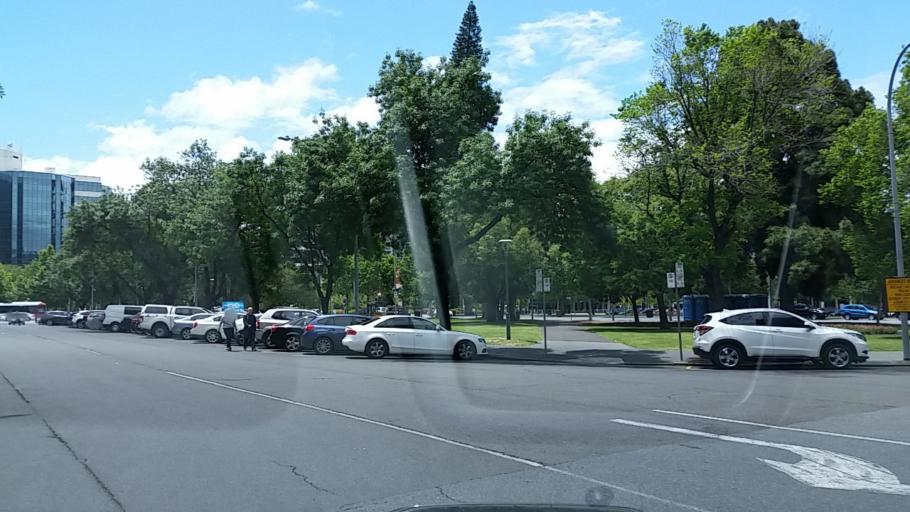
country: AU
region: South Australia
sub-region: Adelaide
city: Adelaide
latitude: -34.9254
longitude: 138.6050
